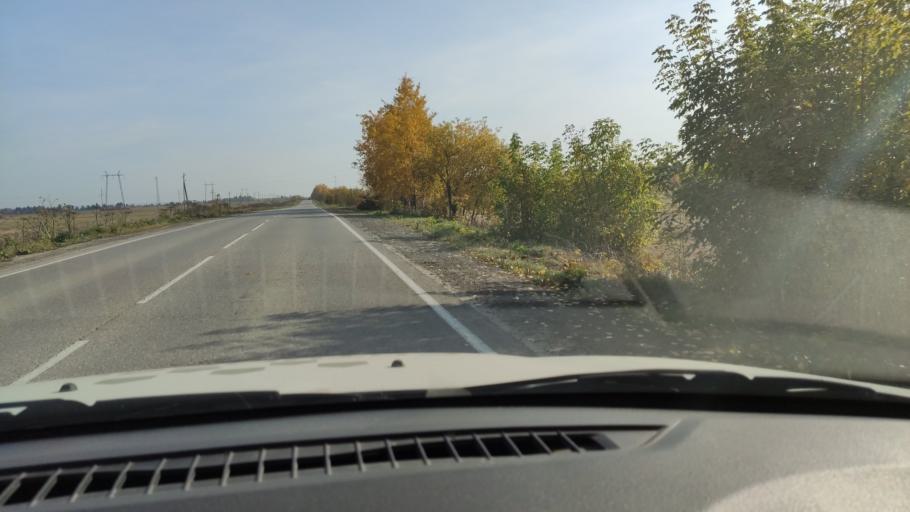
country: RU
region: Perm
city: Sylva
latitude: 58.0299
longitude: 56.6941
